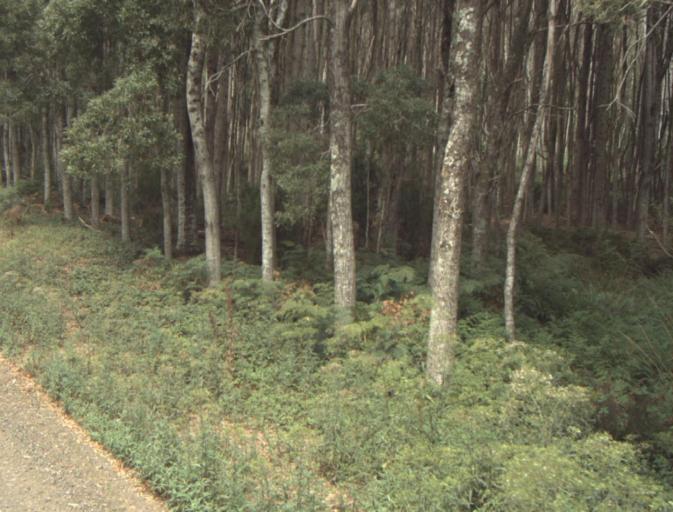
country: AU
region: Tasmania
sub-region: Launceston
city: Mayfield
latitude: -41.1990
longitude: 147.2624
